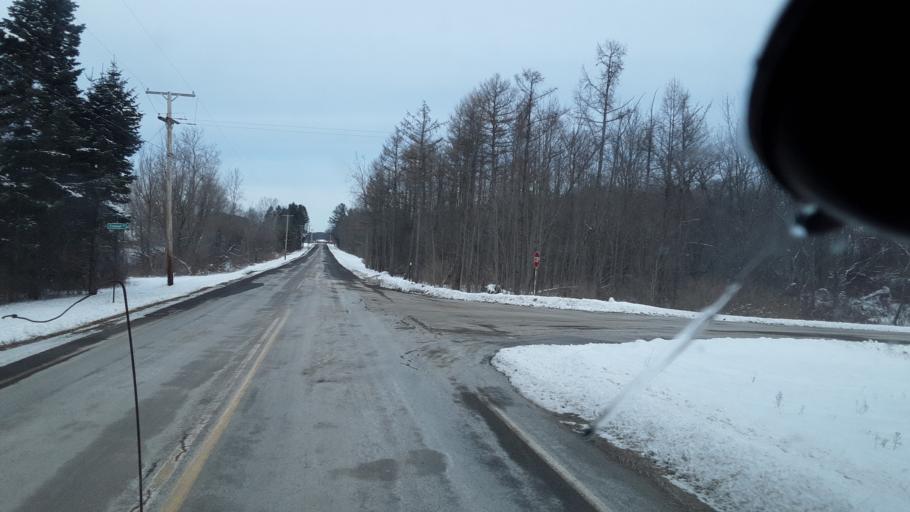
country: US
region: New York
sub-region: Wayne County
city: Lyons
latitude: 43.0997
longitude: -77.0437
